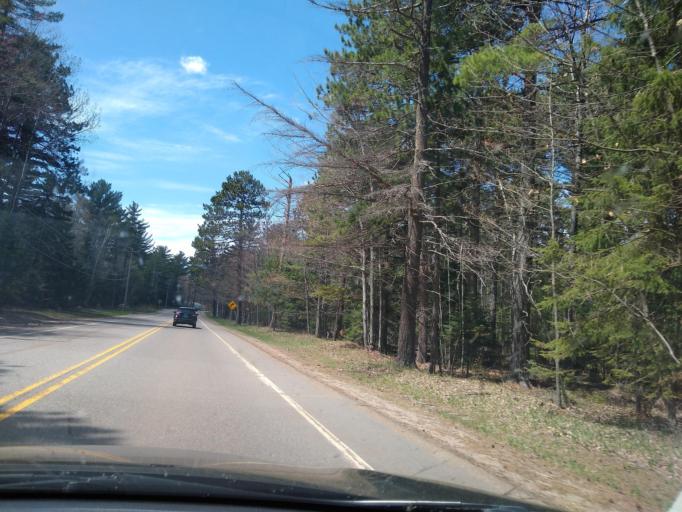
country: US
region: Michigan
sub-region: Marquette County
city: Trowbridge Park
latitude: 46.5732
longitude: -87.4173
